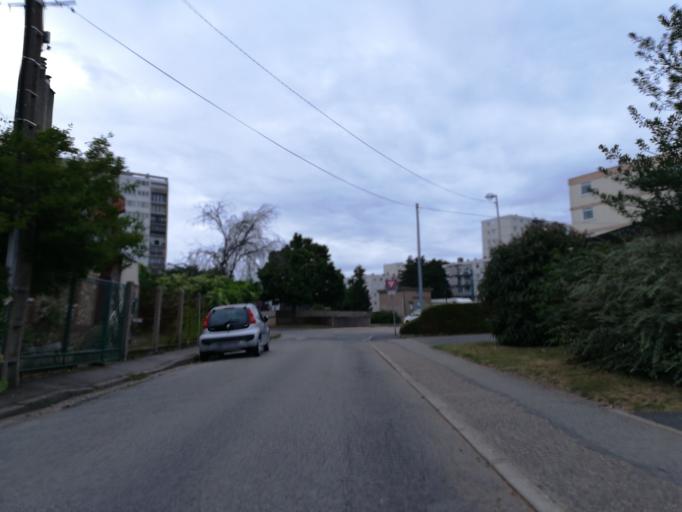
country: FR
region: Haute-Normandie
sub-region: Departement de la Seine-Maritime
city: Mont-Saint-Aignan
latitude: 49.4619
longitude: 1.0736
